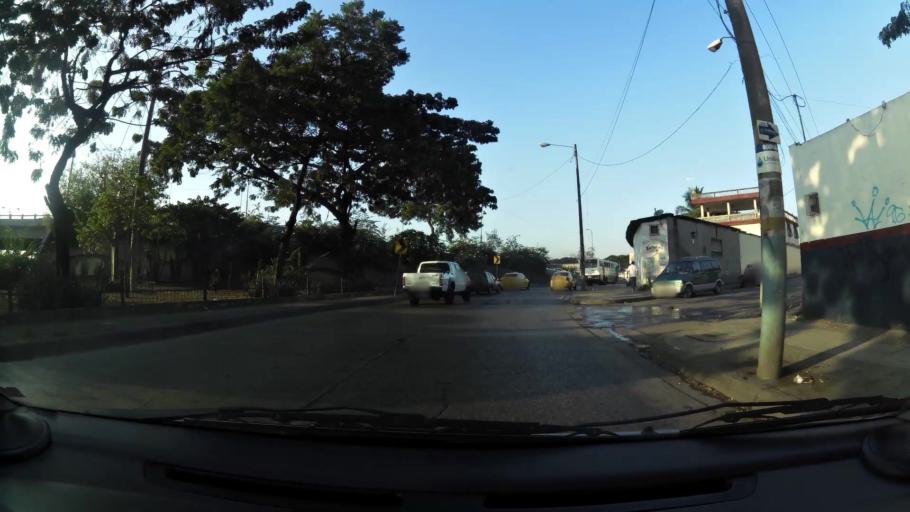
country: EC
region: Guayas
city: Guayaquil
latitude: -2.1405
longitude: -79.9338
